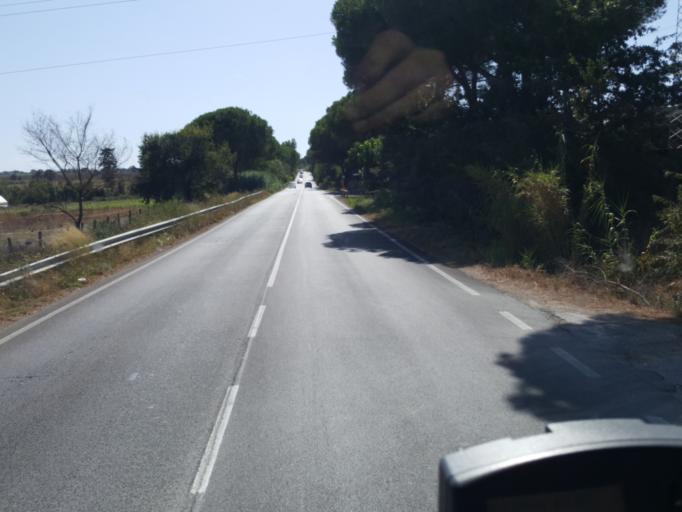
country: IT
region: Latium
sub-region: Provincia di Latina
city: Genio Civile
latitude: 41.5346
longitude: 12.7125
